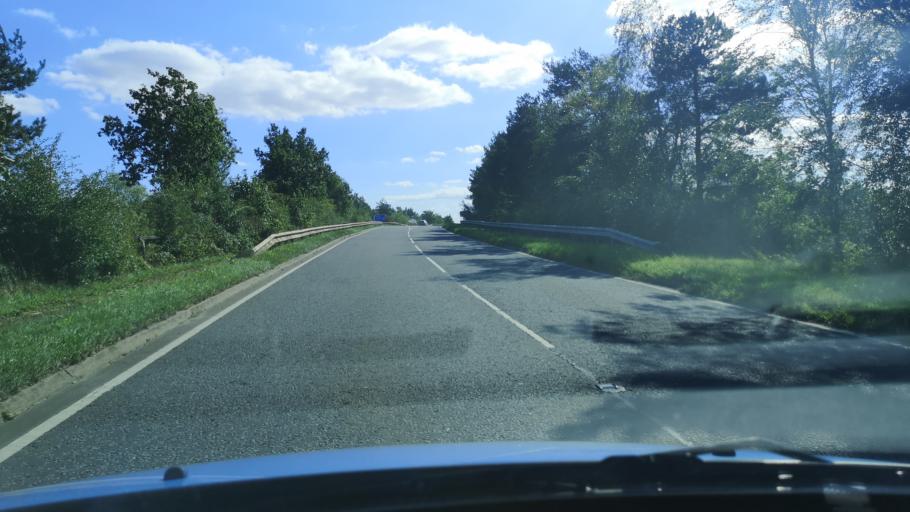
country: GB
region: England
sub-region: North Lincolnshire
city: Belton
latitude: 53.5716
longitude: -0.8176
